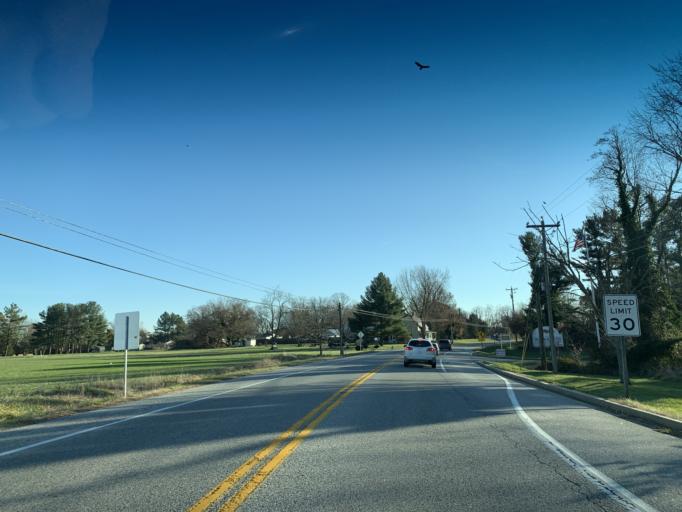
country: US
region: Delaware
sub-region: New Castle County
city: Middletown
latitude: 39.3705
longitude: -75.8830
